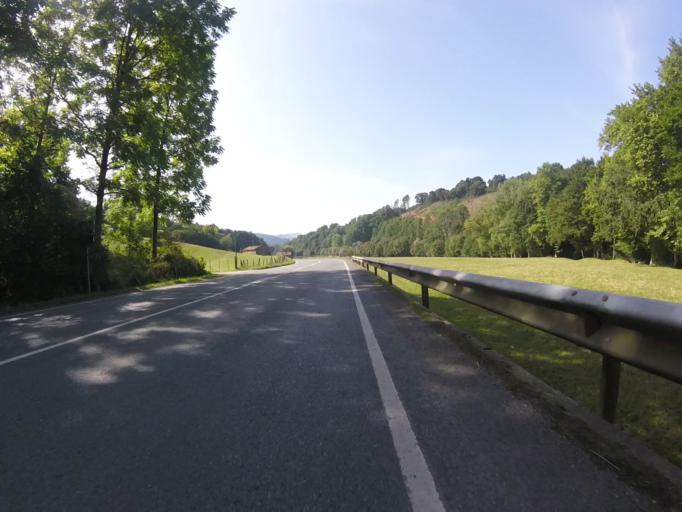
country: ES
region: Navarre
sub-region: Provincia de Navarra
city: Zugarramurdi
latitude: 43.1764
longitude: -1.4927
